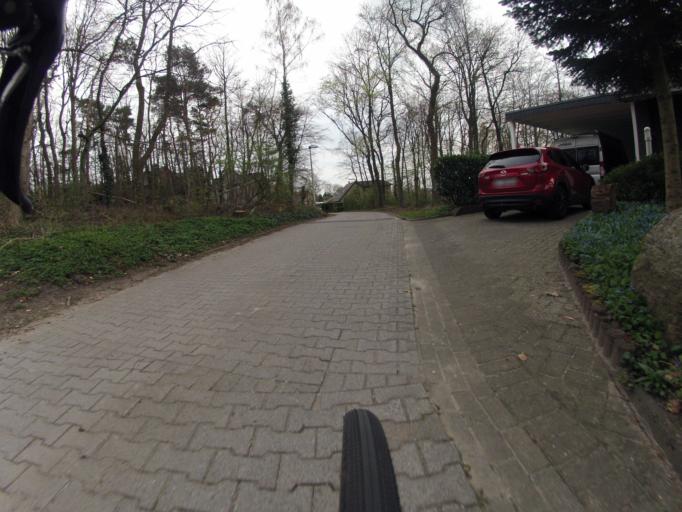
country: DE
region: North Rhine-Westphalia
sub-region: Regierungsbezirk Munster
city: Tecklenburg
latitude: 52.2576
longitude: 7.7840
